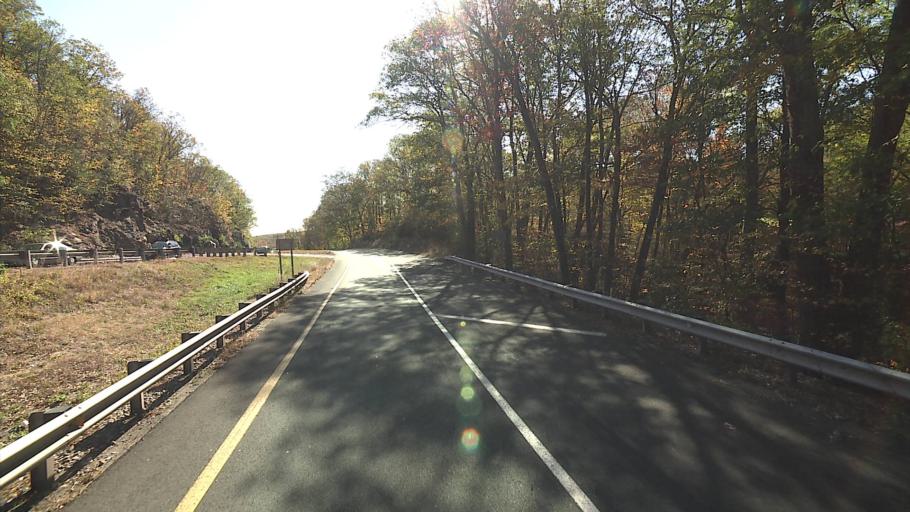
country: US
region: Connecticut
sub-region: Tolland County
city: Rockville
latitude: 41.7883
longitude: -72.4430
